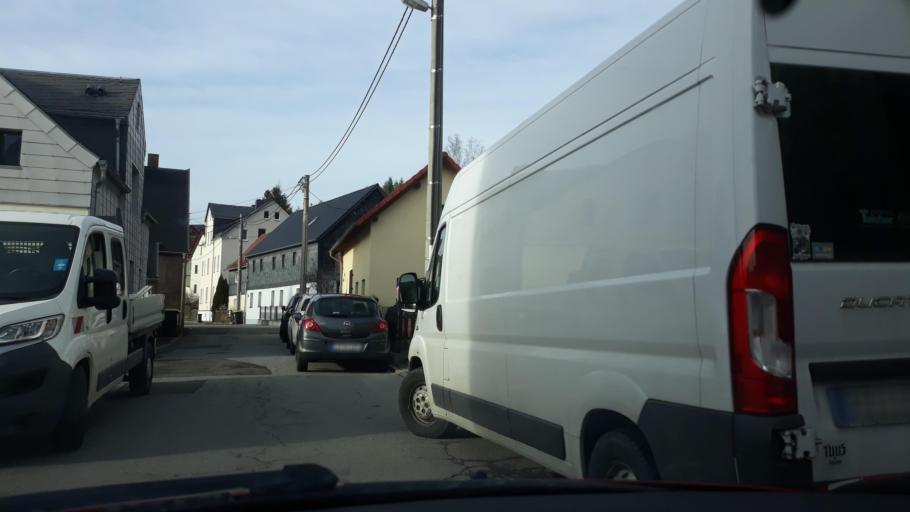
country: DE
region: Saxony
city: Wilkau-Hasslau
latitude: 50.6767
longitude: 12.5229
